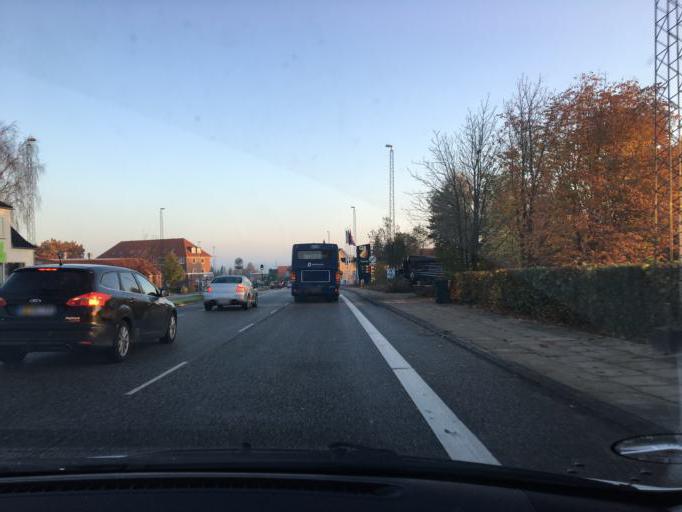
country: DK
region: South Denmark
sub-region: Vejle Kommune
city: Vejle
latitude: 55.6948
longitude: 9.5250
